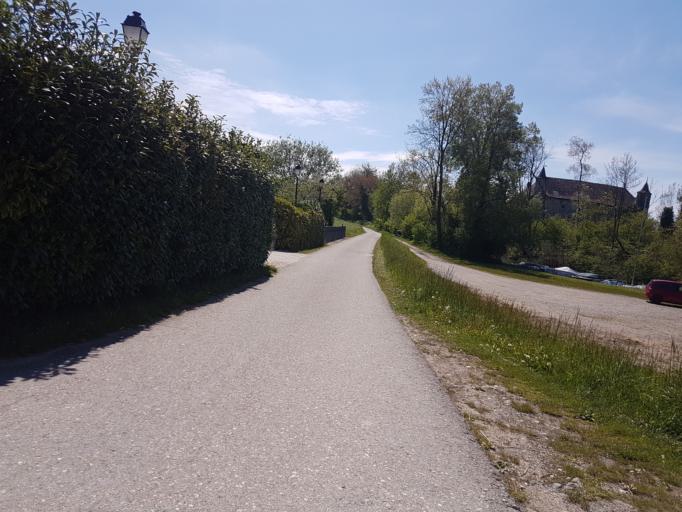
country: CH
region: Neuchatel
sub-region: Neuchatel District
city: Cornaux
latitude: 47.0238
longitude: 7.0340
